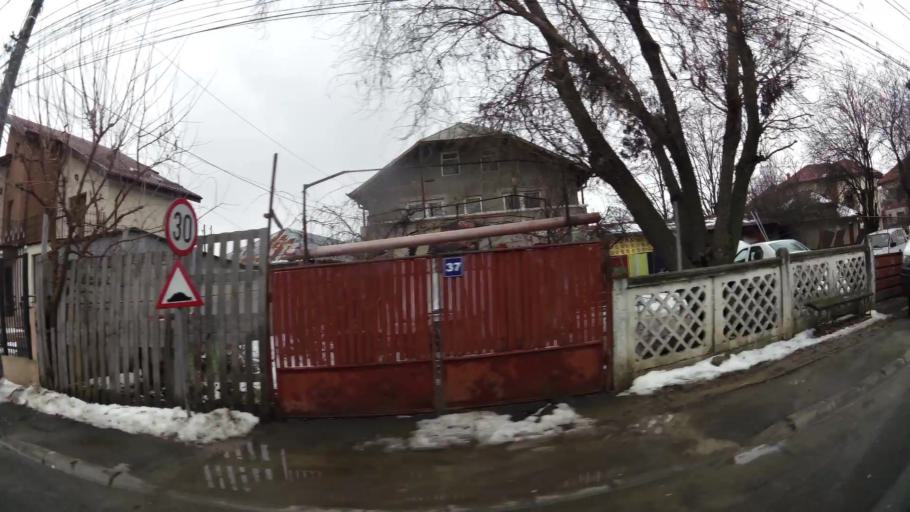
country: RO
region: Ilfov
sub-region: Comuna Otopeni
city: Otopeni
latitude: 44.5480
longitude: 26.0761
